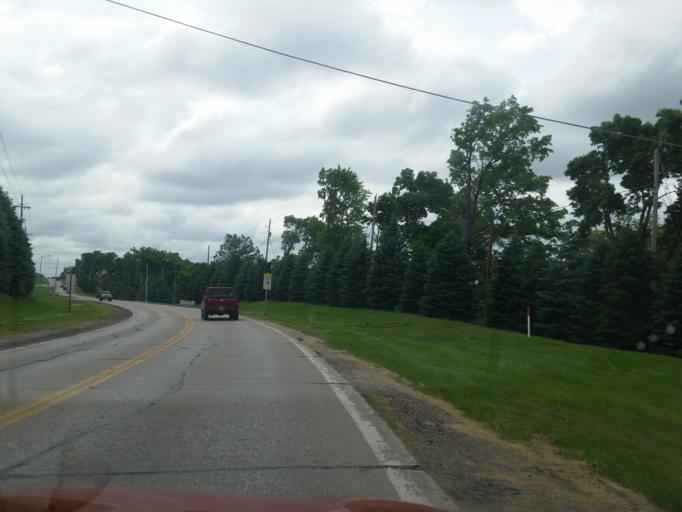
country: US
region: Nebraska
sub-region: Sarpy County
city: Offutt Air Force Base
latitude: 41.1218
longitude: -95.9571
